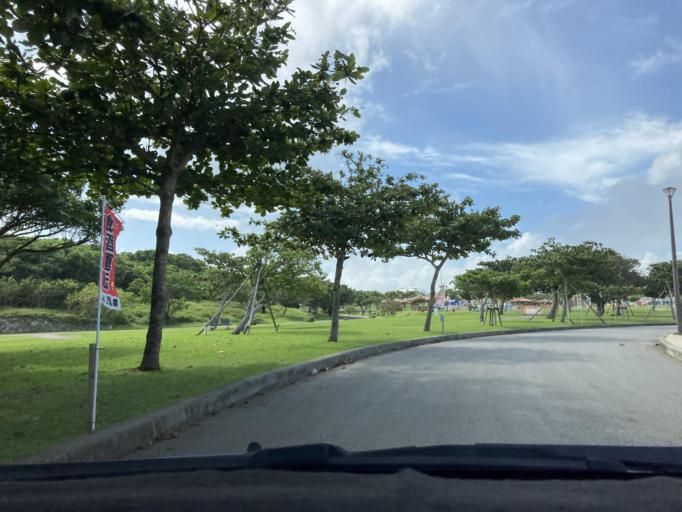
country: JP
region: Okinawa
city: Itoman
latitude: 26.0990
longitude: 127.7251
